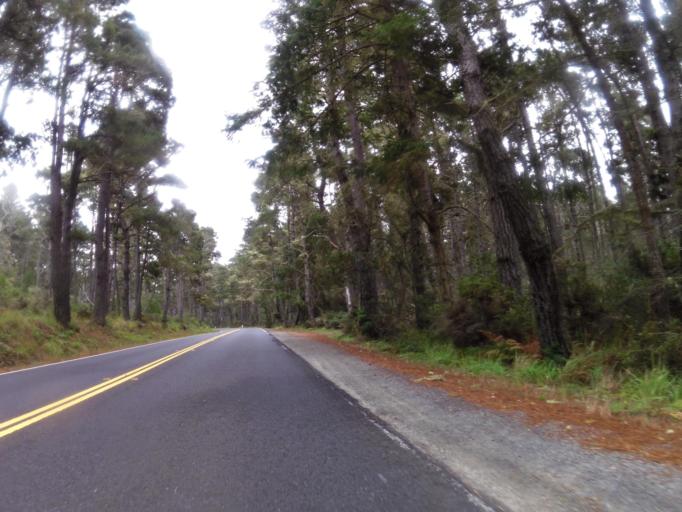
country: US
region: California
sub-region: Sonoma County
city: Sea Ranch
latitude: 38.5649
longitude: -123.3183
